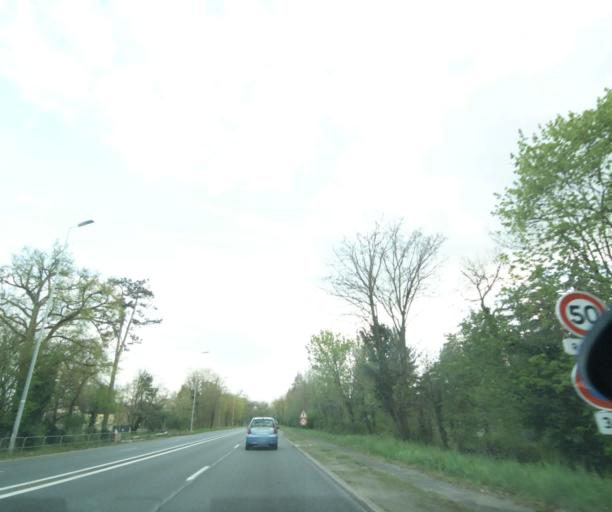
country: FR
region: Ile-de-France
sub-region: Departement de Seine-et-Marne
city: Fontainebleau
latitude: 48.4037
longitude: 2.6870
